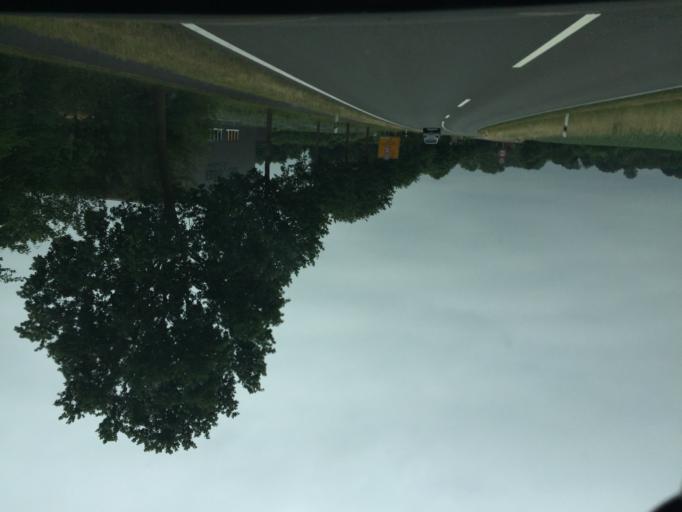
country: DE
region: North Rhine-Westphalia
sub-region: Regierungsbezirk Munster
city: Ostbevern
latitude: 52.1149
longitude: 7.8472
